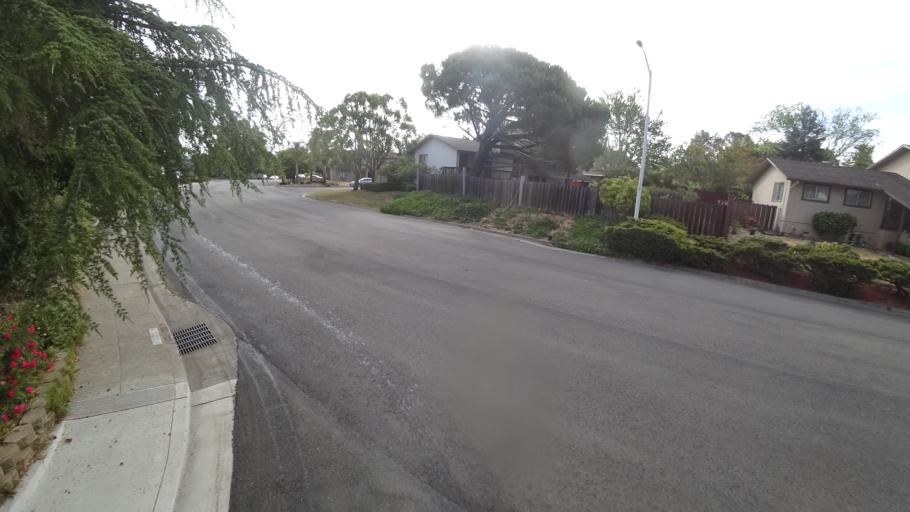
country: US
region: California
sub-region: Alameda County
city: Fairview
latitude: 37.6544
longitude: -122.0379
